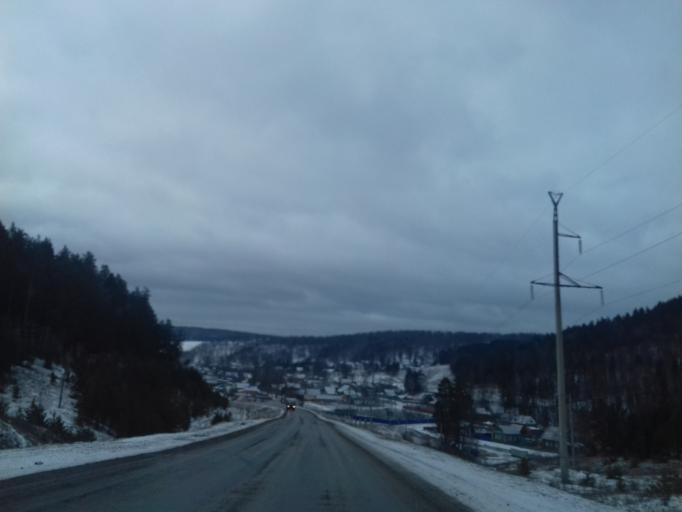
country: RU
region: Bashkortostan
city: Starosubkhangulovo
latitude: 53.1282
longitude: 57.4150
